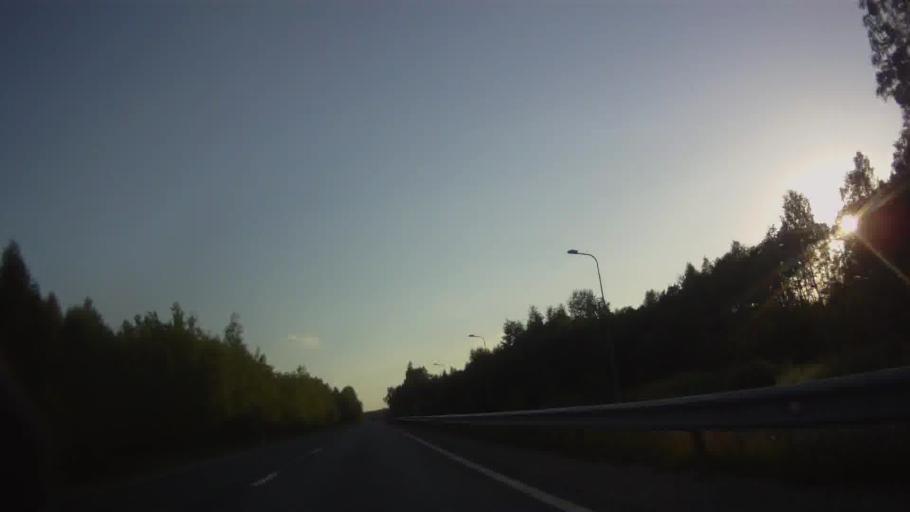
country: LV
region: Livani
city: Livani
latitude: 56.5426
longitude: 26.0856
